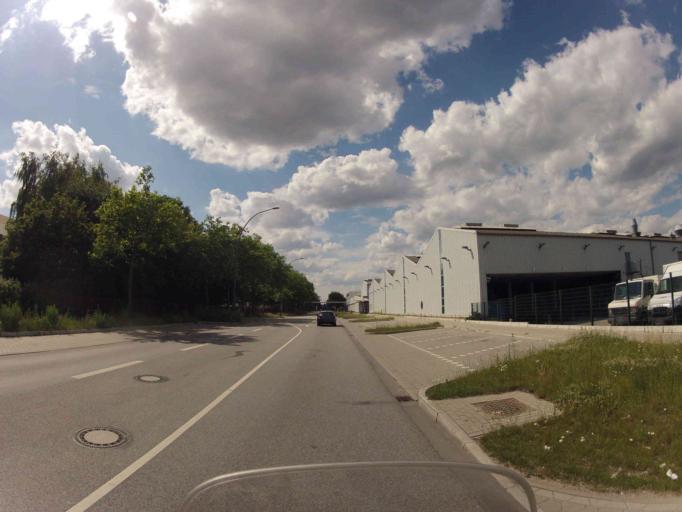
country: DE
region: Hamburg
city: Marienthal
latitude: 53.5325
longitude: 10.0774
